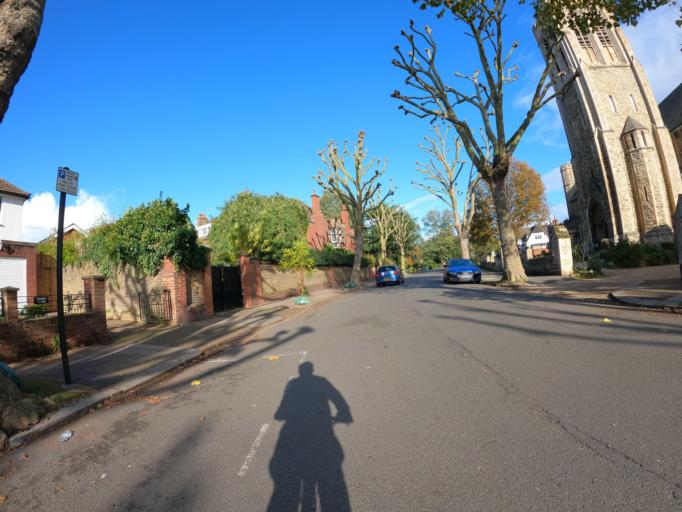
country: GB
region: England
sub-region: Greater London
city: Ealing
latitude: 51.5071
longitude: -0.2959
